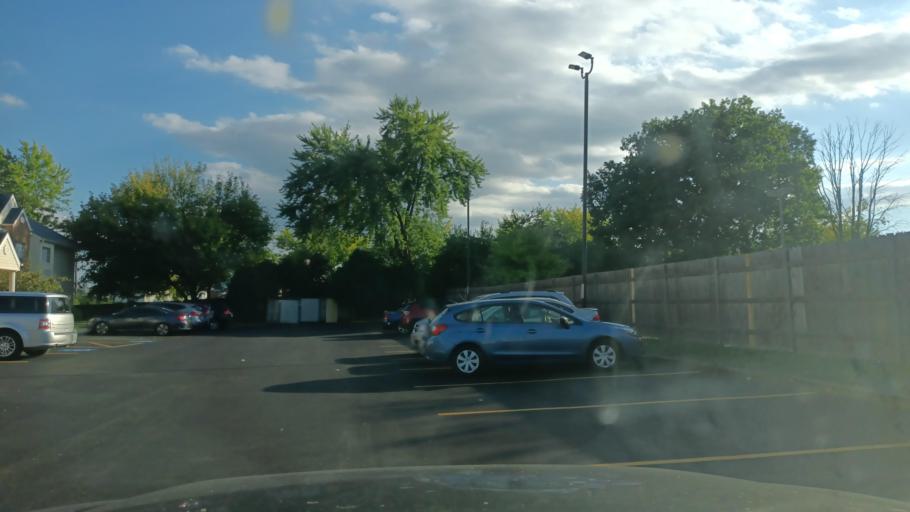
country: US
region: Ohio
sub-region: Montgomery County
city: Riverside
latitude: 39.7430
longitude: -84.1149
